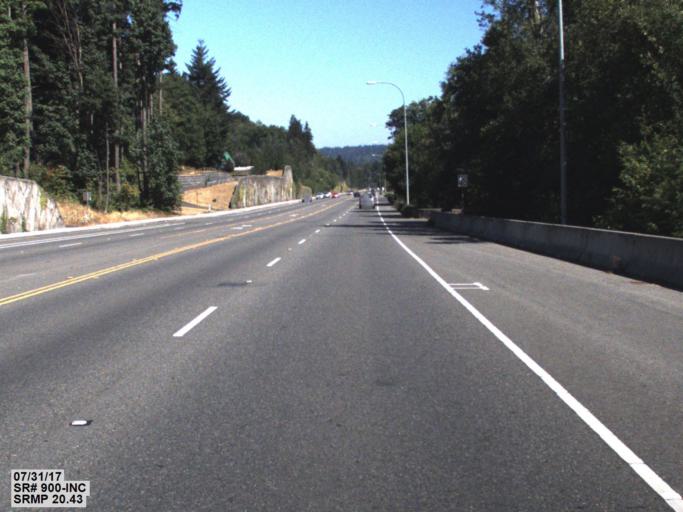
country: US
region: Washington
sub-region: King County
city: Issaquah
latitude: 47.5318
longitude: -122.0620
